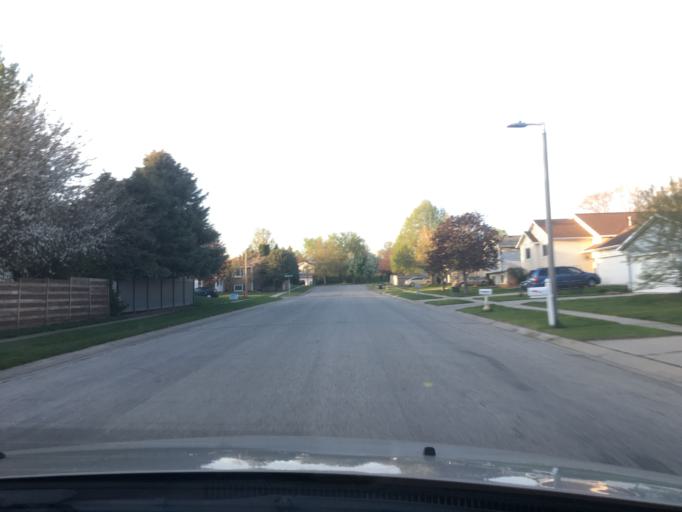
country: US
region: Minnesota
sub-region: Olmsted County
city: Oronoco
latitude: 44.0833
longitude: -92.5270
